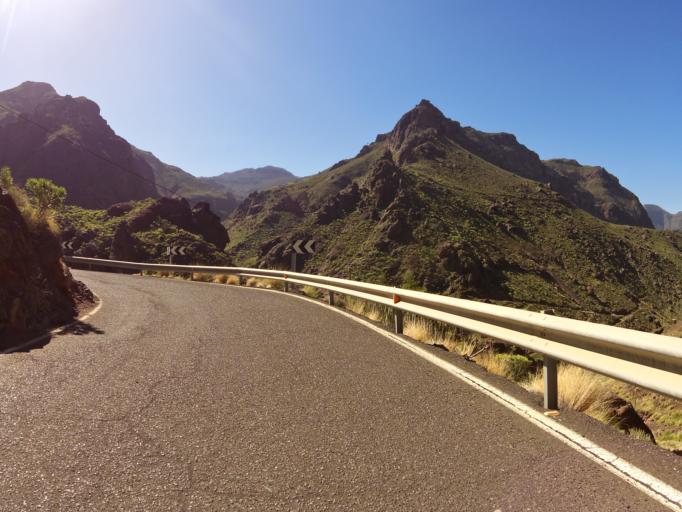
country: ES
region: Canary Islands
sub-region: Provincia de Las Palmas
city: San Nicolas
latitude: 27.9894
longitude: -15.7492
